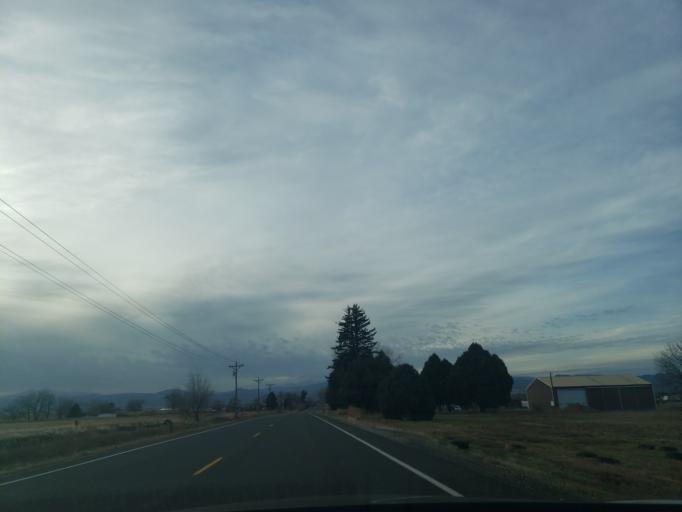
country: US
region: Colorado
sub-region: Weld County
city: Windsor
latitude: 40.4648
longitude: -104.9976
